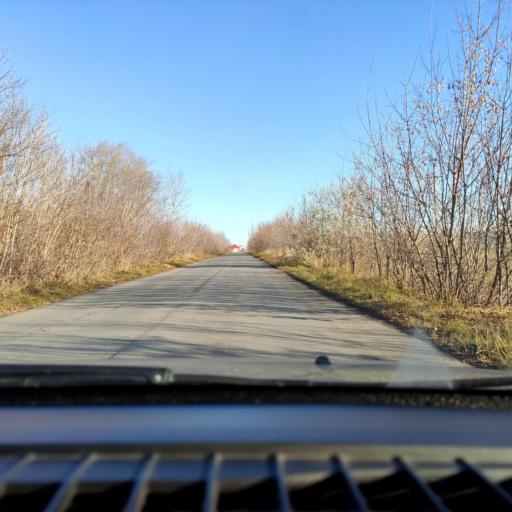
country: RU
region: Samara
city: Tol'yatti
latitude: 53.6619
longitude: 49.3348
